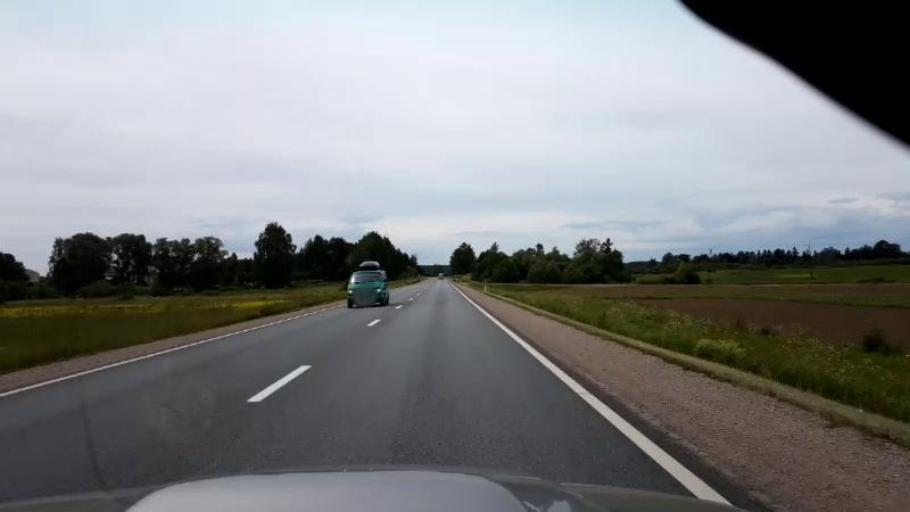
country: LV
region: Bauskas Rajons
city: Bauska
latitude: 56.4697
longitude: 24.1652
